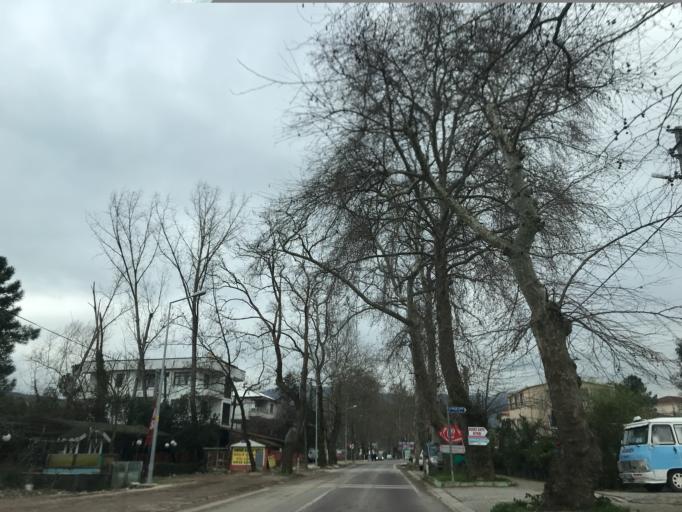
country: TR
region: Yalova
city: Kadikoy
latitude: 40.6119
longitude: 29.2113
